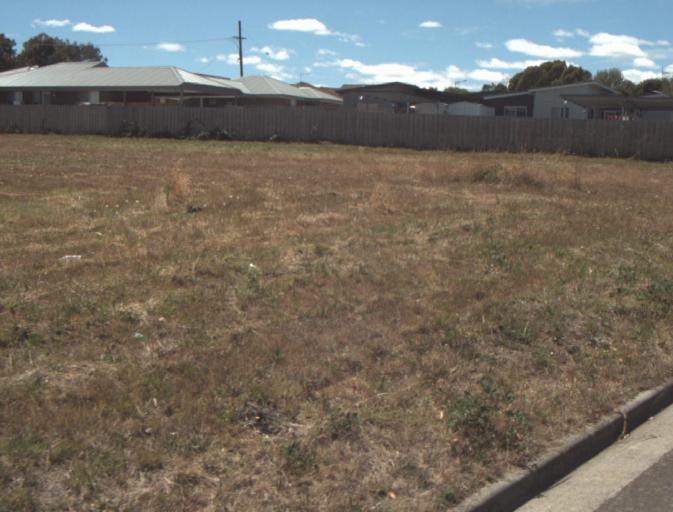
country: AU
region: Tasmania
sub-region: Launceston
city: Mayfield
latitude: -41.3782
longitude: 147.1343
